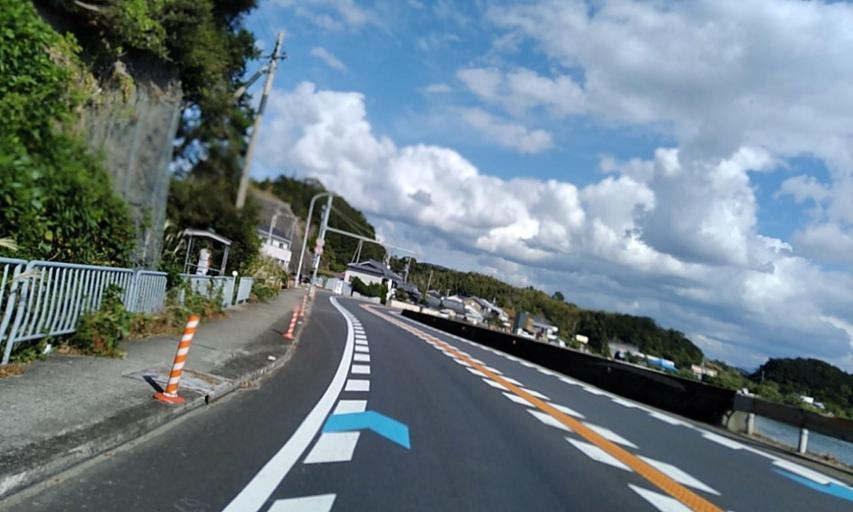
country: JP
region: Wakayama
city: Tanabe
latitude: 33.7458
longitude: 135.3404
